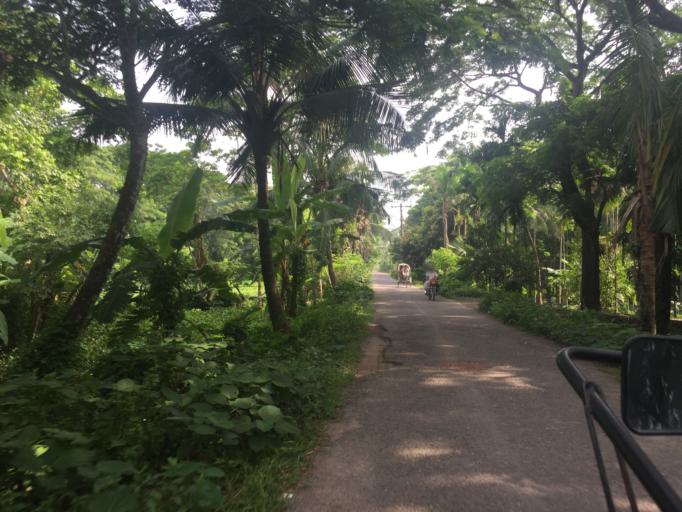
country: BD
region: Barisal
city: Mathba
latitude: 22.2237
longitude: 89.9162
